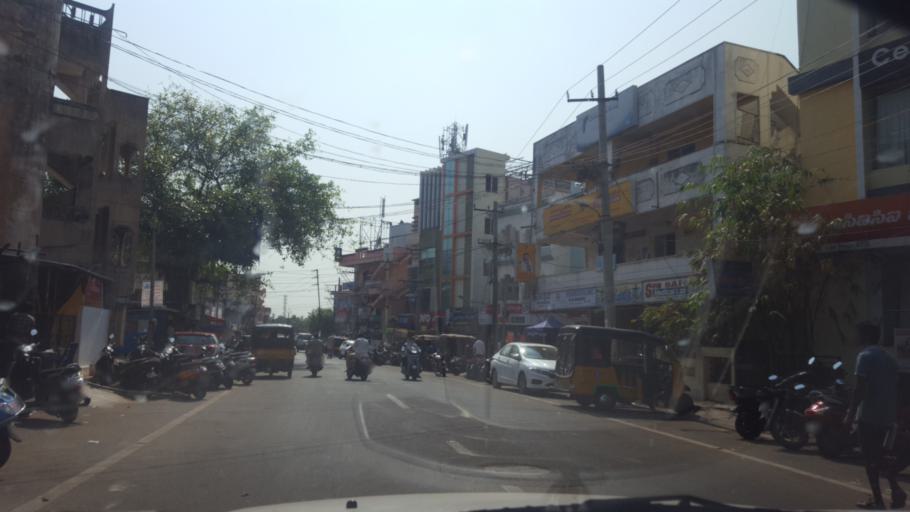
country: IN
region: Andhra Pradesh
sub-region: Vishakhapatnam
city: Vepagunta
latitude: 17.7449
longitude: 83.2588
